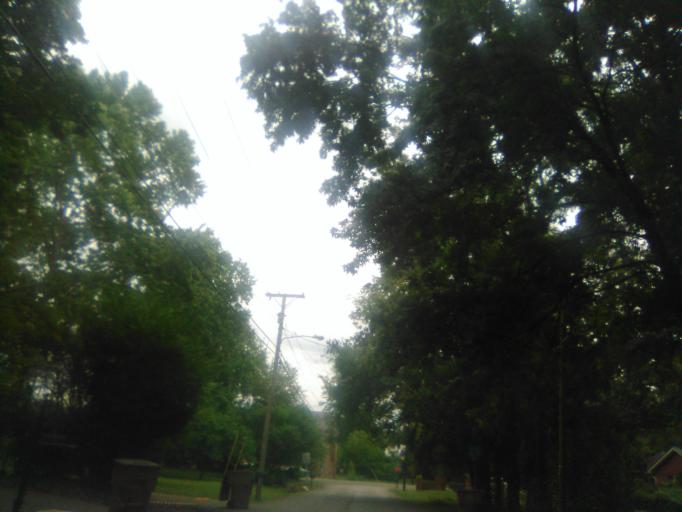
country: US
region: Tennessee
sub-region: Davidson County
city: Belle Meade
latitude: 36.1009
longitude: -86.8738
